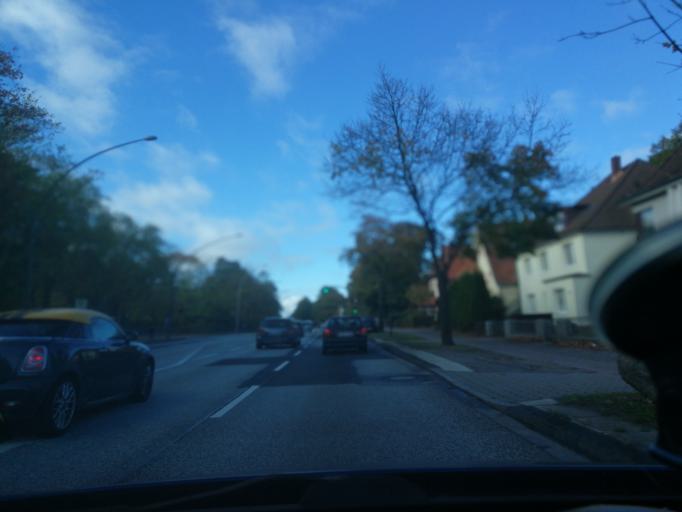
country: DE
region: Lower Saxony
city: Neu Wulmstorf
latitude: 53.4721
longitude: 9.8849
